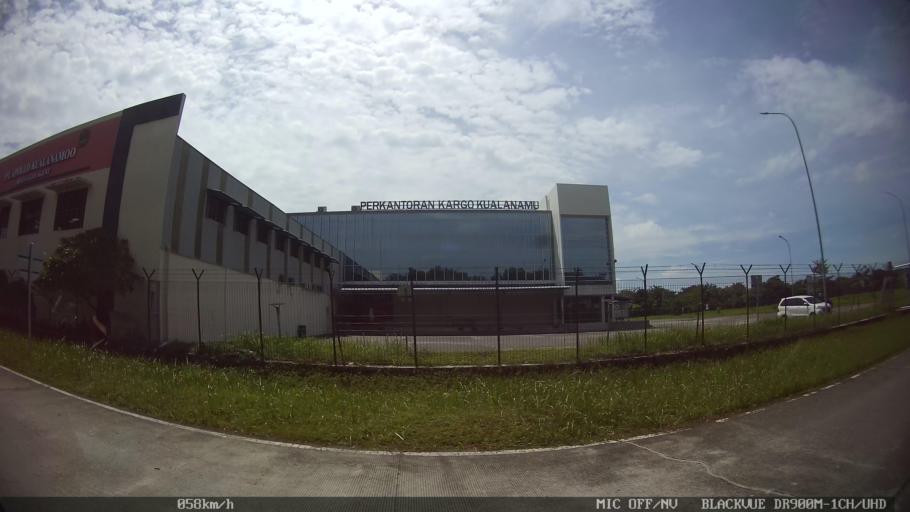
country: ID
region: North Sumatra
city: Percut
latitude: 3.6253
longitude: 98.8667
